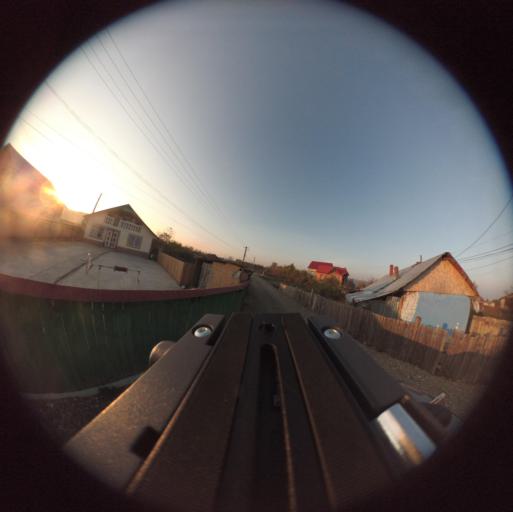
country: RO
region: Vaslui
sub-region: Comuna Bacesti
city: Bacesti
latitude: 46.8277
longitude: 27.2506
